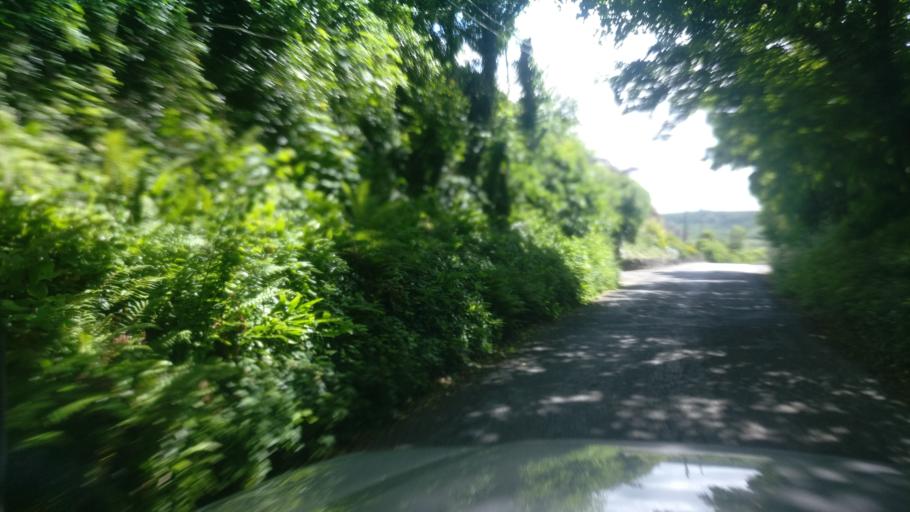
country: IE
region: Connaught
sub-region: County Galway
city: Gort
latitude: 53.1371
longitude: -8.7183
